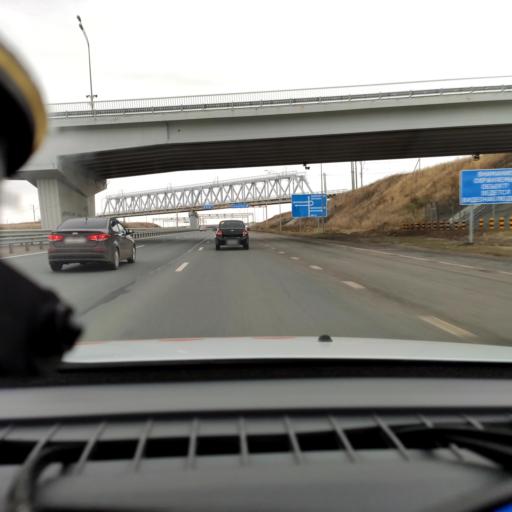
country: RU
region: Samara
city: Smyshlyayevka
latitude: 53.1488
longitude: 50.3821
